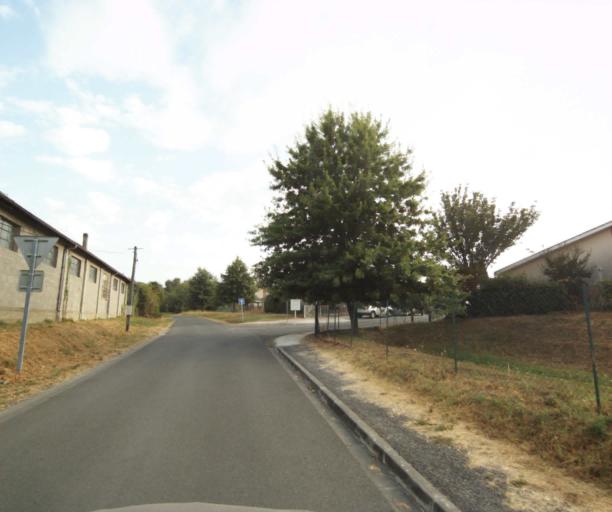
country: FR
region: Aquitaine
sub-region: Departement de la Gironde
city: Creon
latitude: 44.7779
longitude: -0.3503
